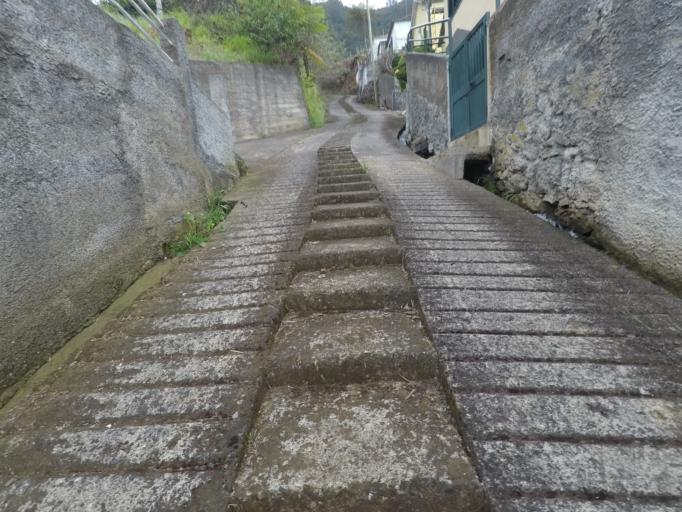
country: PT
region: Madeira
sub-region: Santana
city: Santana
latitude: 32.7884
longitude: -16.8572
